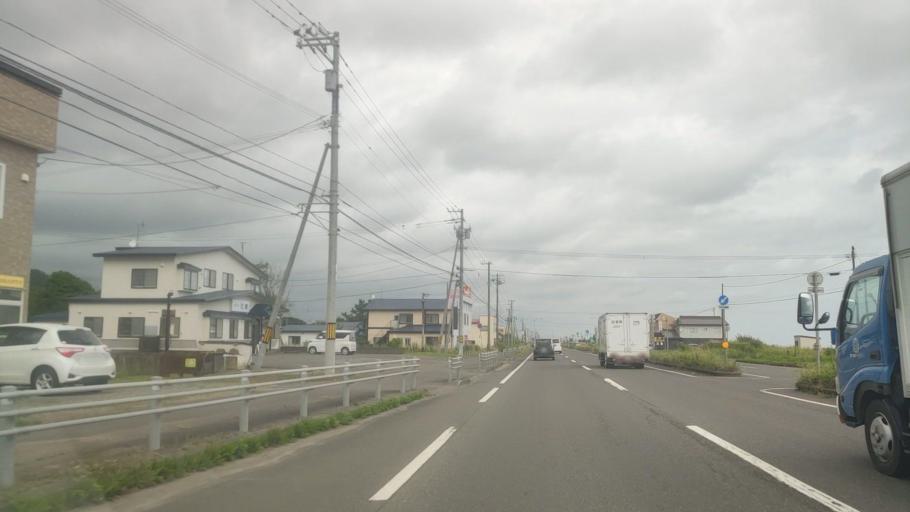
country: JP
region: Hokkaido
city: Shiraoi
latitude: 42.4686
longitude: 141.2275
